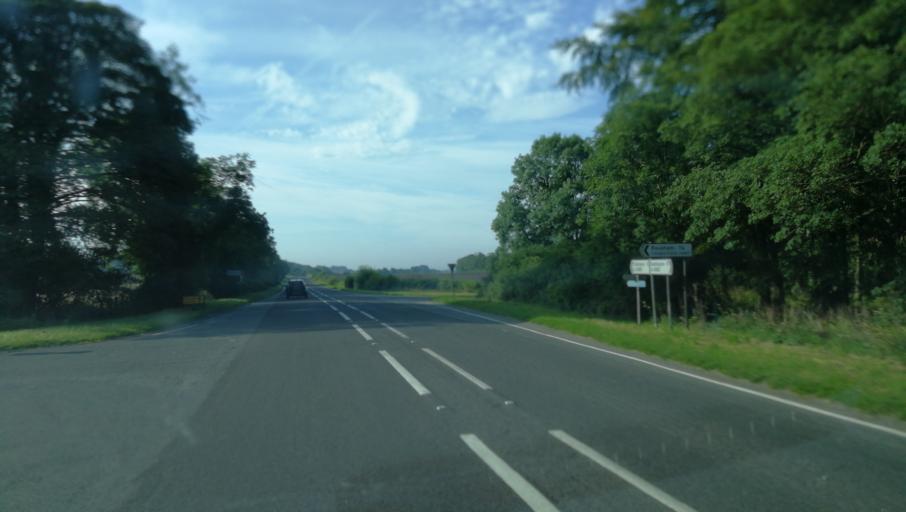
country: GB
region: England
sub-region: Oxfordshire
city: Woodstock
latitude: 51.8992
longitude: -1.3286
